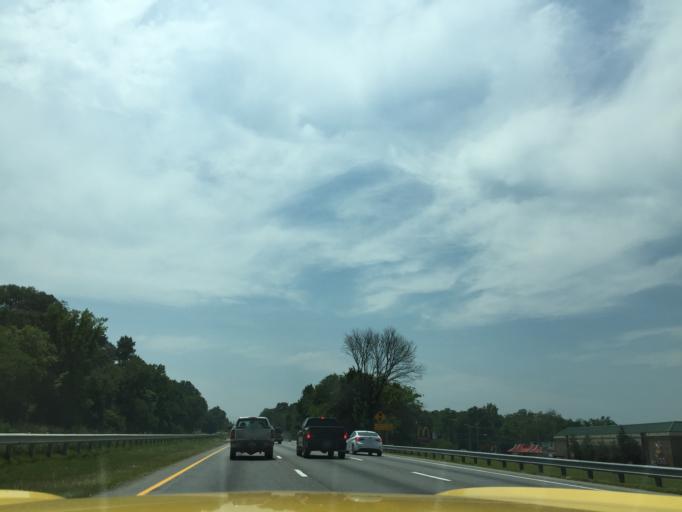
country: US
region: Maryland
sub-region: Prince George's County
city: Friendly
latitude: 38.7587
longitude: -76.9936
